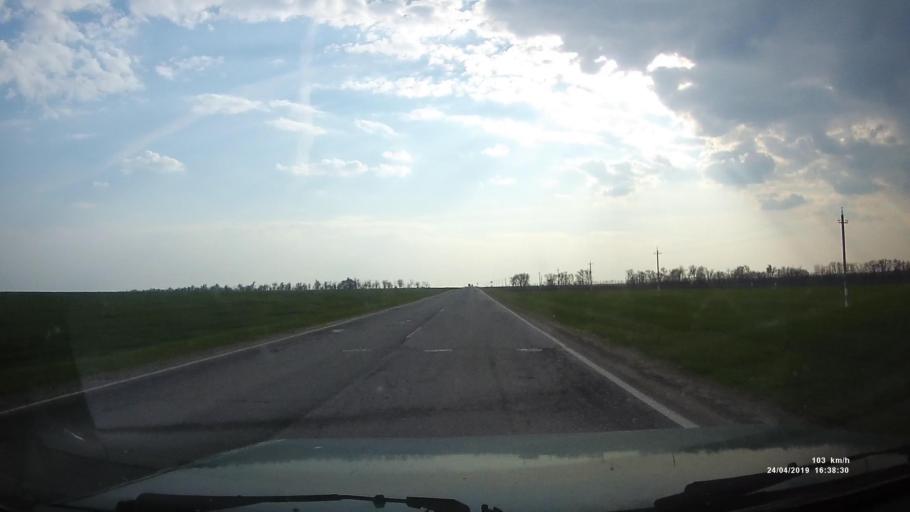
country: RU
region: Rostov
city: Gundorovskiy
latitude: 46.8494
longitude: 41.9140
